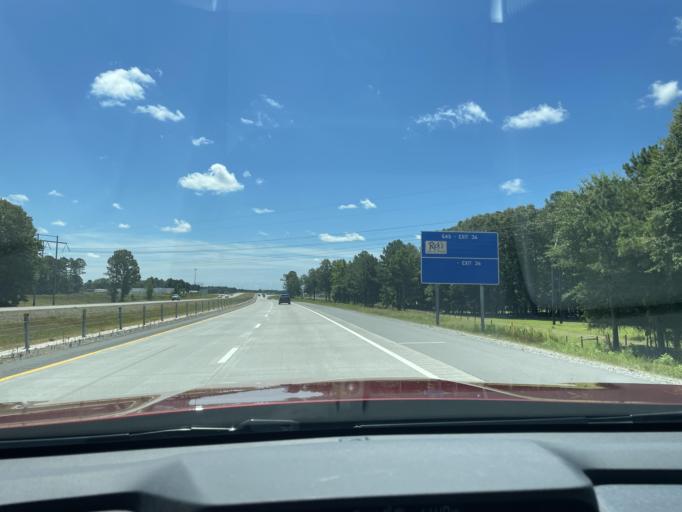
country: US
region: Arkansas
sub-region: Jefferson County
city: White Hall
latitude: 34.2343
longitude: -92.0843
